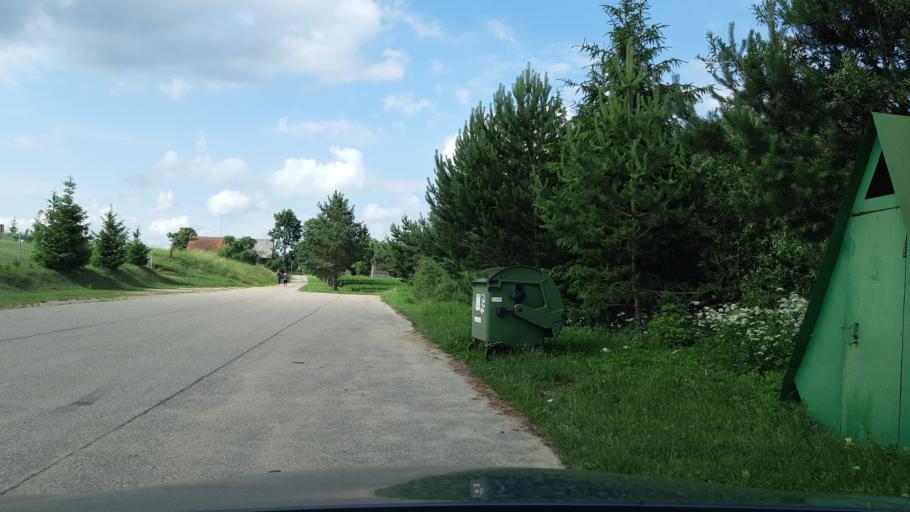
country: LT
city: Kybartai
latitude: 54.4524
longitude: 22.7204
